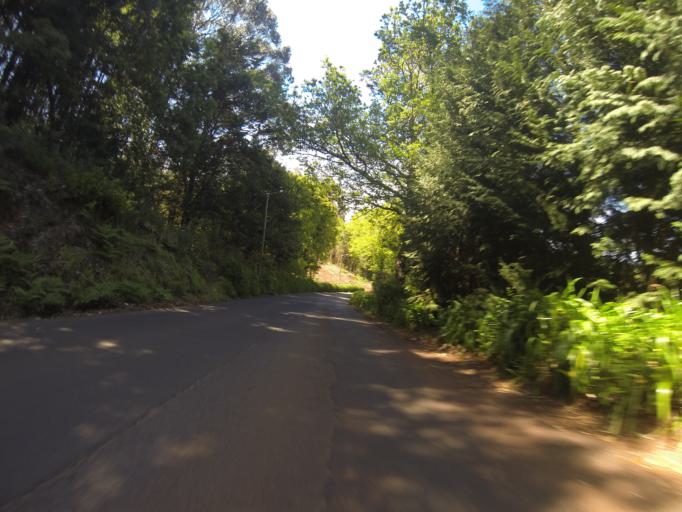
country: PT
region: Madeira
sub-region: Santa Cruz
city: Santa Cruz
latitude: 32.7254
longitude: -16.8249
